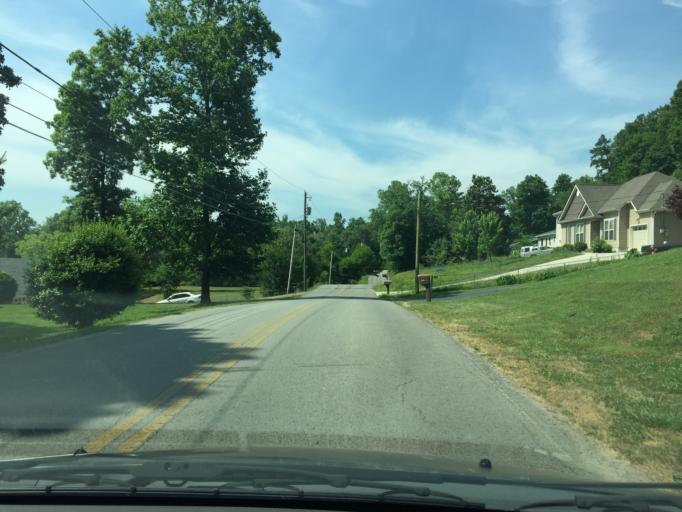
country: US
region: Tennessee
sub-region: Hamilton County
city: Collegedale
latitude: 35.0642
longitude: -85.0464
